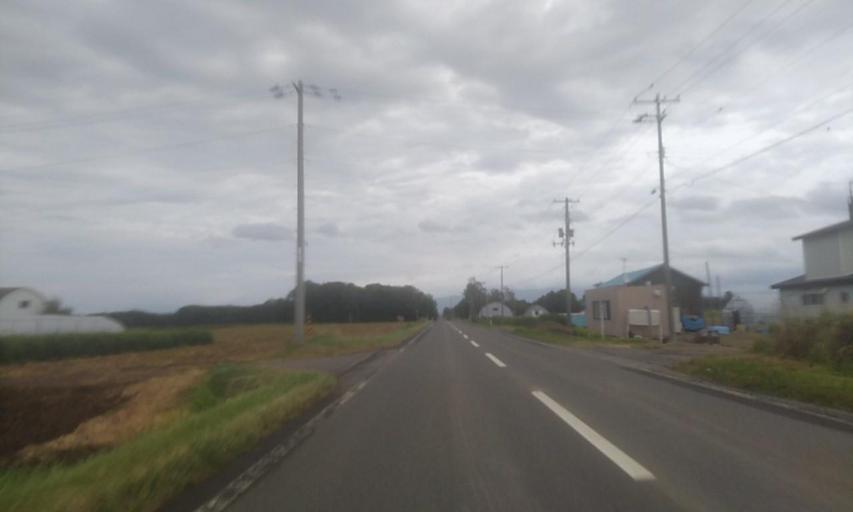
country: JP
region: Hokkaido
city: Abashiri
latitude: 43.8956
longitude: 144.5543
